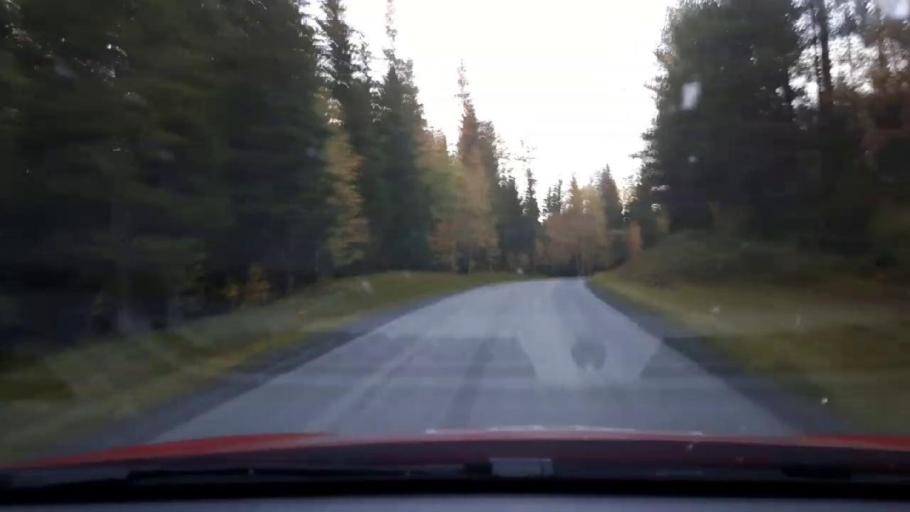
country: SE
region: Jaemtland
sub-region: Krokoms Kommun
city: Krokom
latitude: 63.4709
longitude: 14.3421
